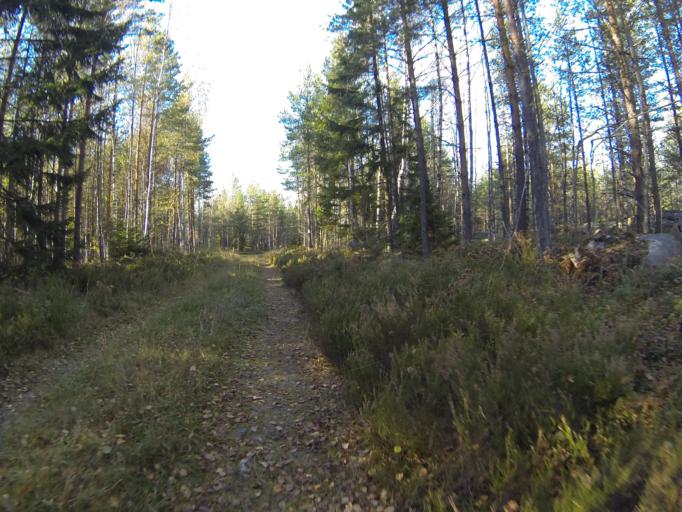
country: FI
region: Varsinais-Suomi
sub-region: Salo
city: Saerkisalo
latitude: 60.2246
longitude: 22.9594
